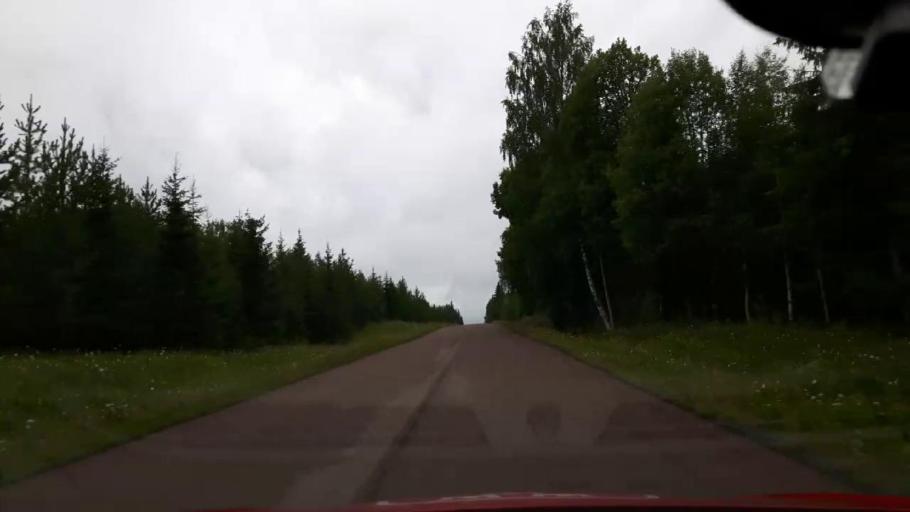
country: SE
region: Jaemtland
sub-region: Krokoms Kommun
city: Valla
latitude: 63.3686
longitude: 13.7492
